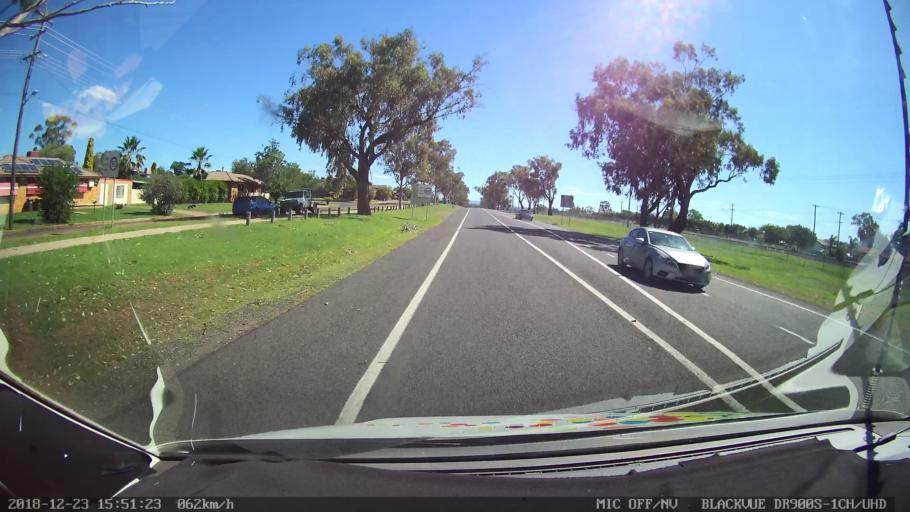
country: AU
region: New South Wales
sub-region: Tamworth Municipality
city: South Tamworth
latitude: -31.1124
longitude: 150.8962
